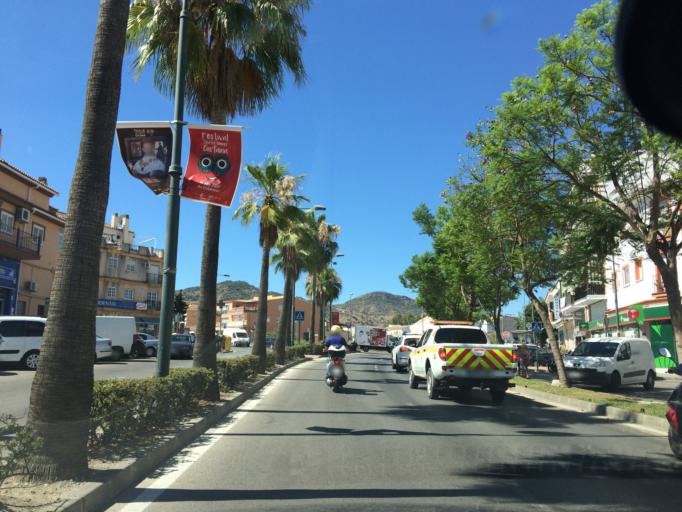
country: ES
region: Andalusia
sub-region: Provincia de Malaga
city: Estacion de Cartama
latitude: 36.7336
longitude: -4.6128
